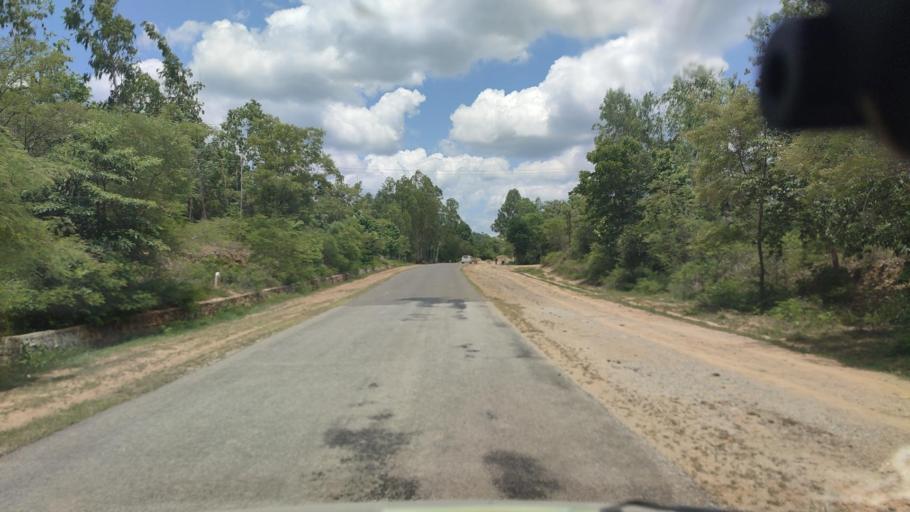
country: MM
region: Magway
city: Taungdwingyi
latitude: 20.1455
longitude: 95.6331
